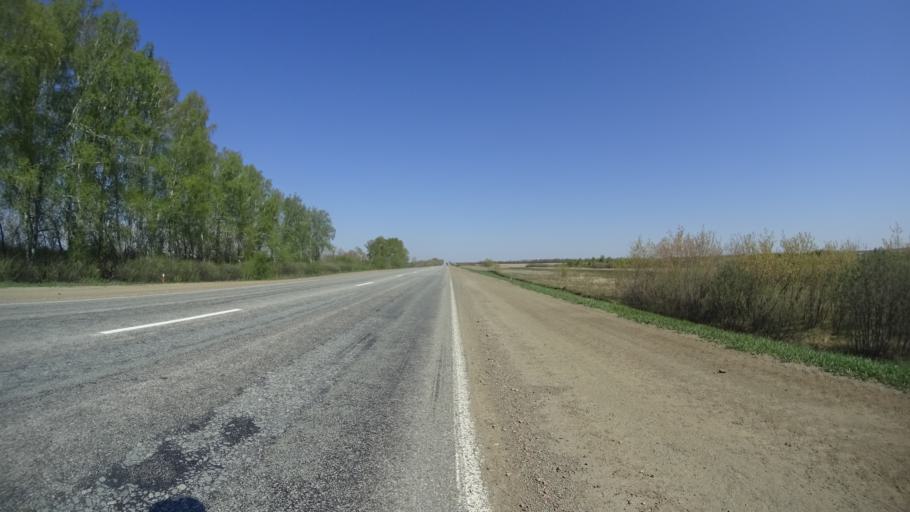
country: RU
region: Chelyabinsk
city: Troitsk
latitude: 54.1993
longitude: 61.4324
